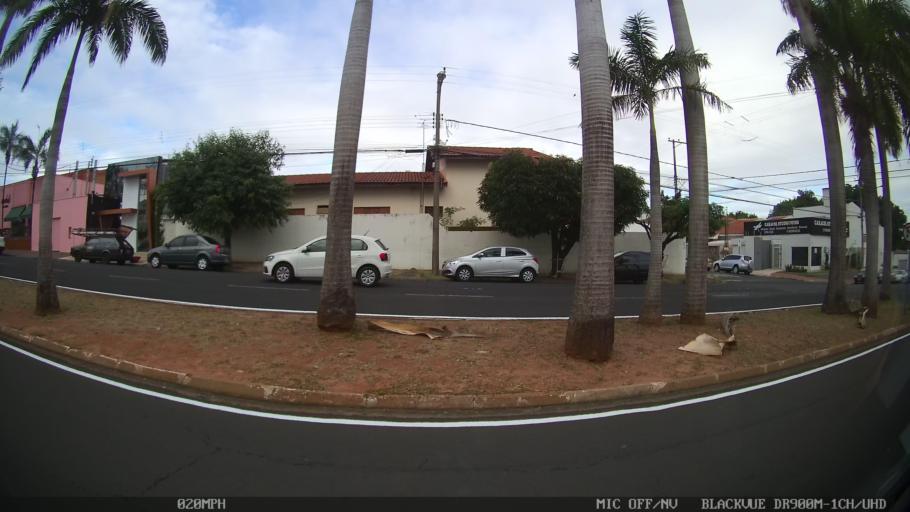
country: BR
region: Sao Paulo
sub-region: Sao Jose Do Rio Preto
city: Sao Jose do Rio Preto
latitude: -20.8322
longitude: -49.4022
